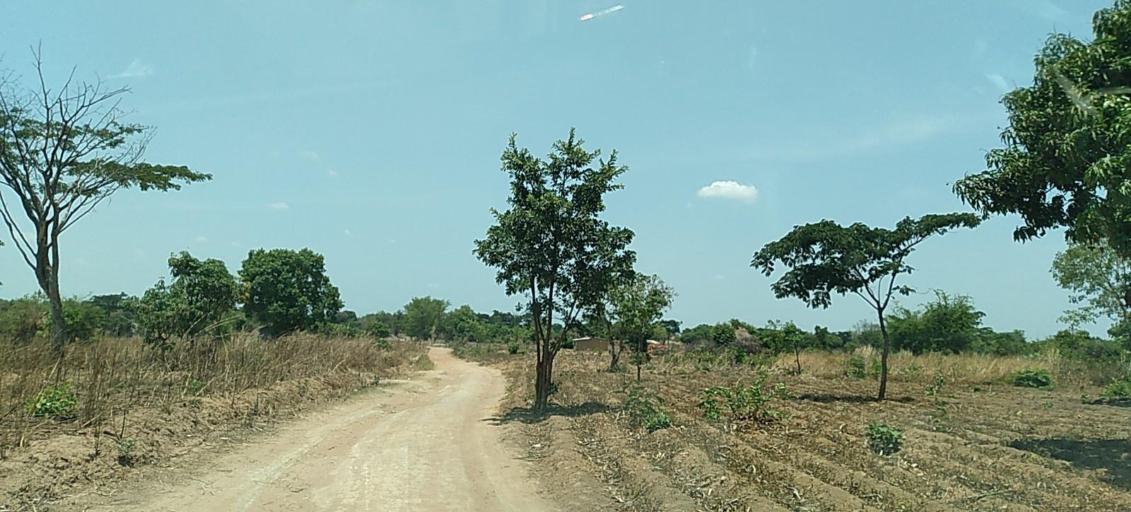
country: ZM
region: Copperbelt
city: Luanshya
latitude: -13.0718
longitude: 28.4062
